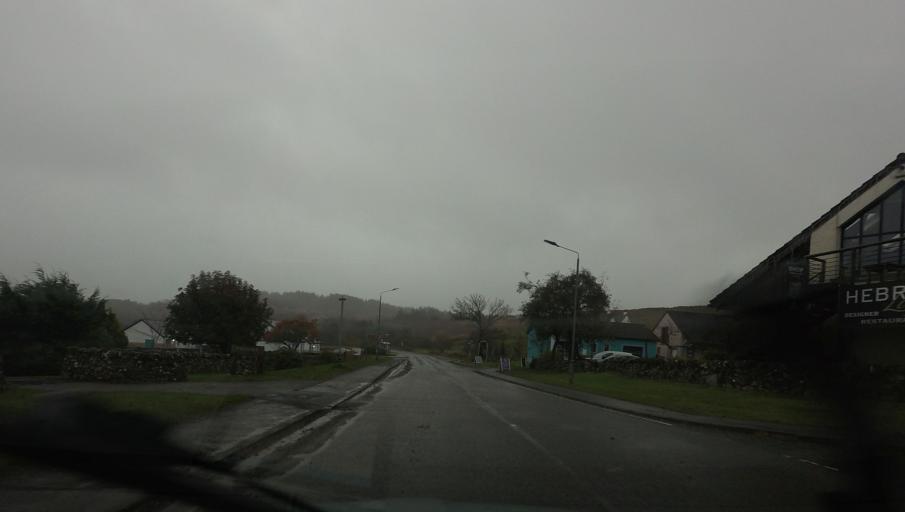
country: GB
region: Scotland
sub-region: Argyll and Bute
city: Isle Of Mull
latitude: 56.6152
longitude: -6.0710
